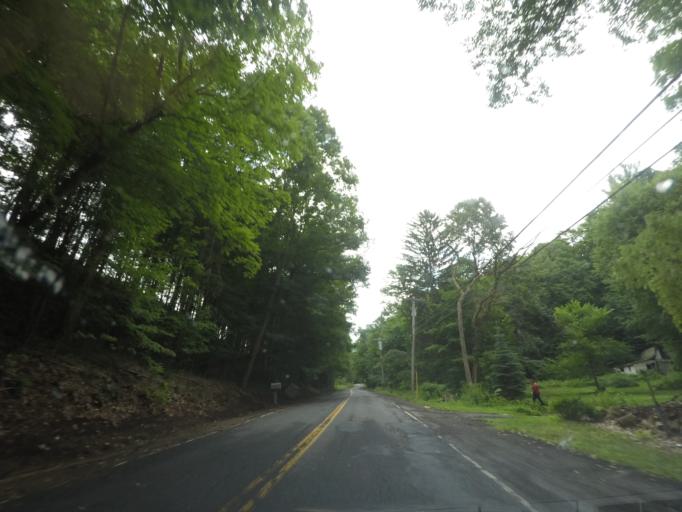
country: US
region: New York
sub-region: Rensselaer County
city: West Sand Lake
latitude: 42.6700
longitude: -73.6143
